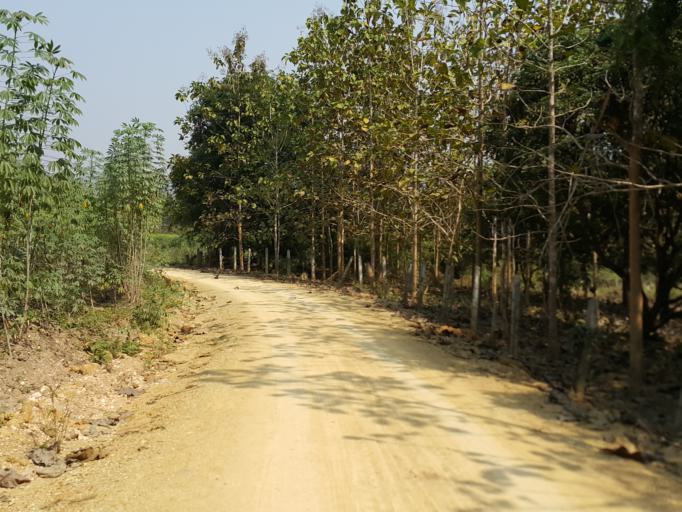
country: TH
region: Sukhothai
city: Thung Saliam
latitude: 17.3331
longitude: 99.4598
